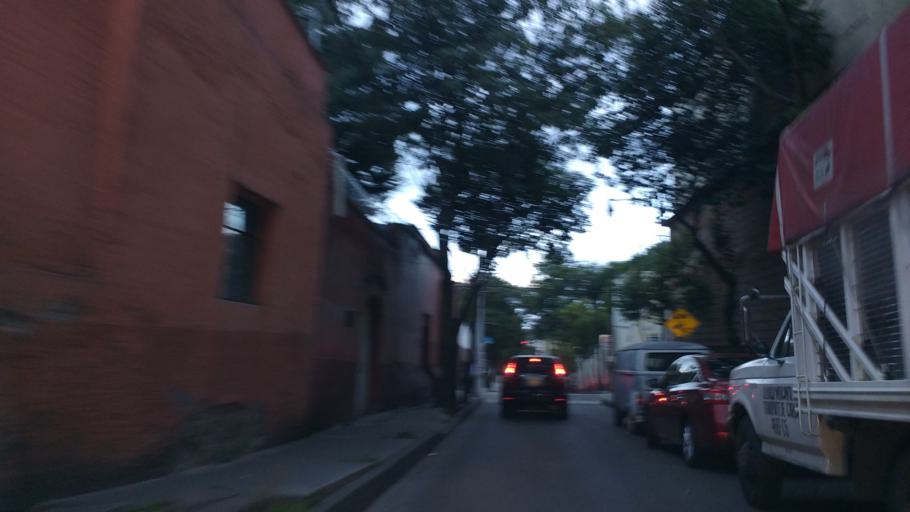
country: MX
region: Mexico City
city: Tlalpan
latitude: 19.2871
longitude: -99.1646
